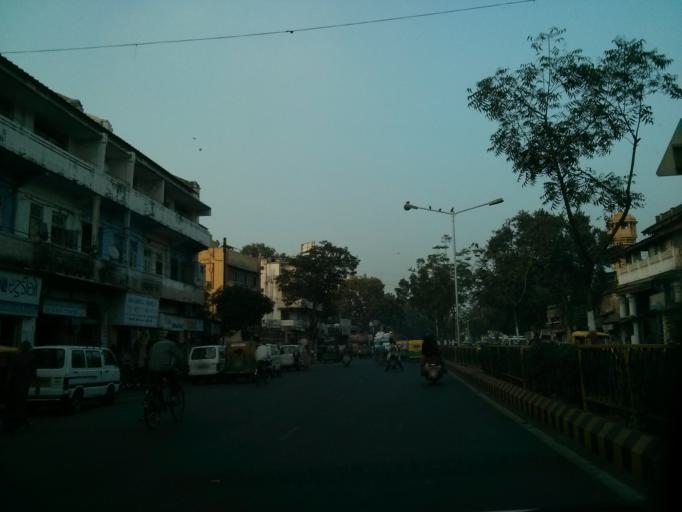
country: IN
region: Gujarat
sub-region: Ahmadabad
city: Ahmedabad
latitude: 23.0404
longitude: 72.5885
